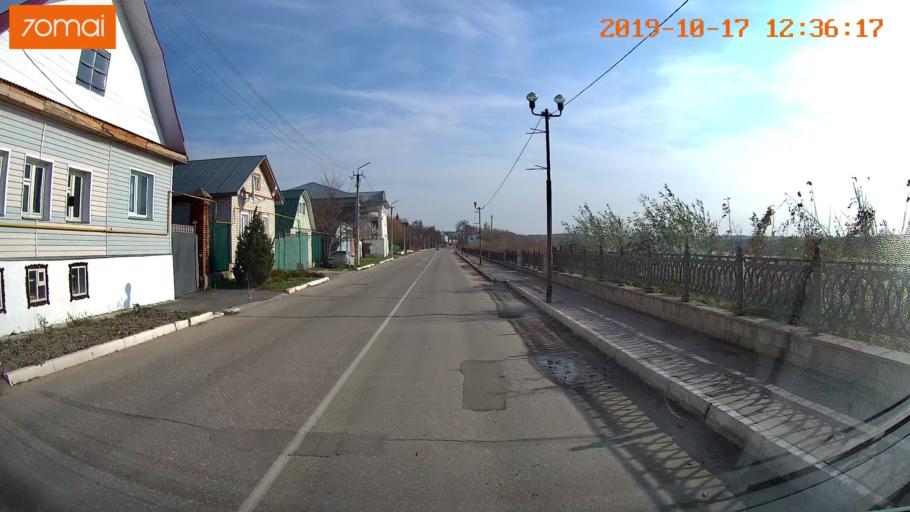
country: RU
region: Rjazan
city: Kasimov
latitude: 54.9404
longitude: 41.3741
